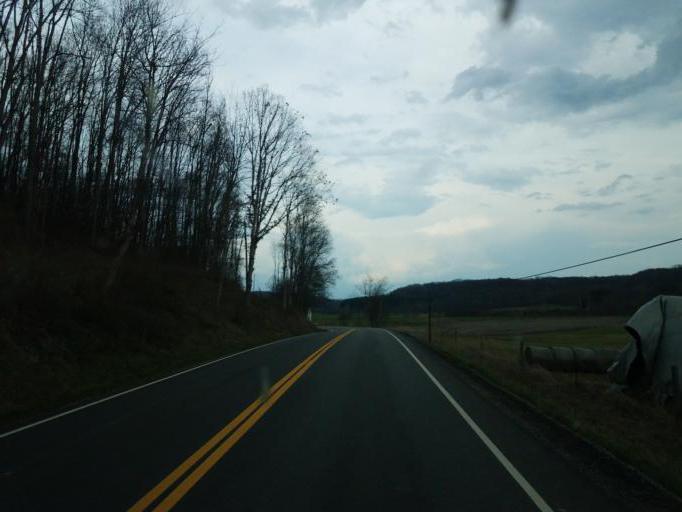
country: US
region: Ohio
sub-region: Guernsey County
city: Mantua
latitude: 40.1089
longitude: -81.7744
